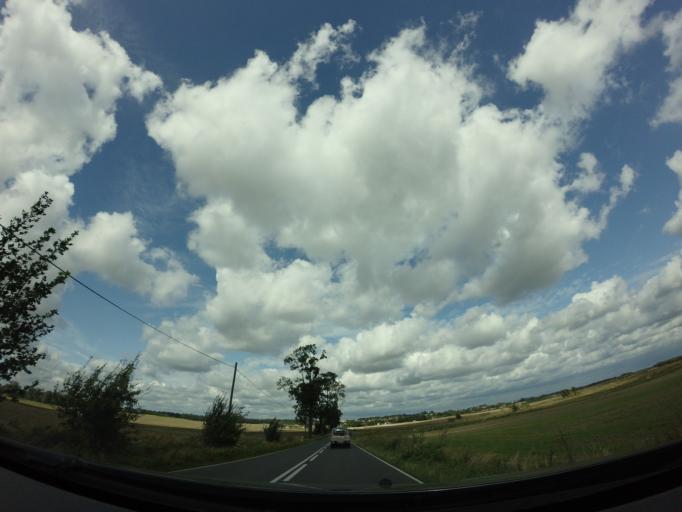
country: PL
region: Lubusz
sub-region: Powiat strzelecko-drezdenecki
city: Dobiegniew
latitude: 52.9506
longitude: 15.7512
